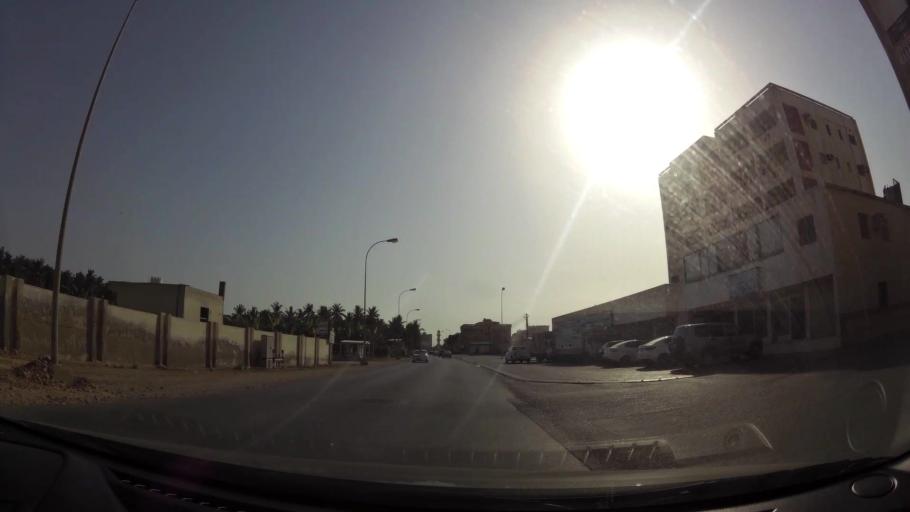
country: OM
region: Zufar
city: Salalah
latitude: 17.0083
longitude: 54.0849
